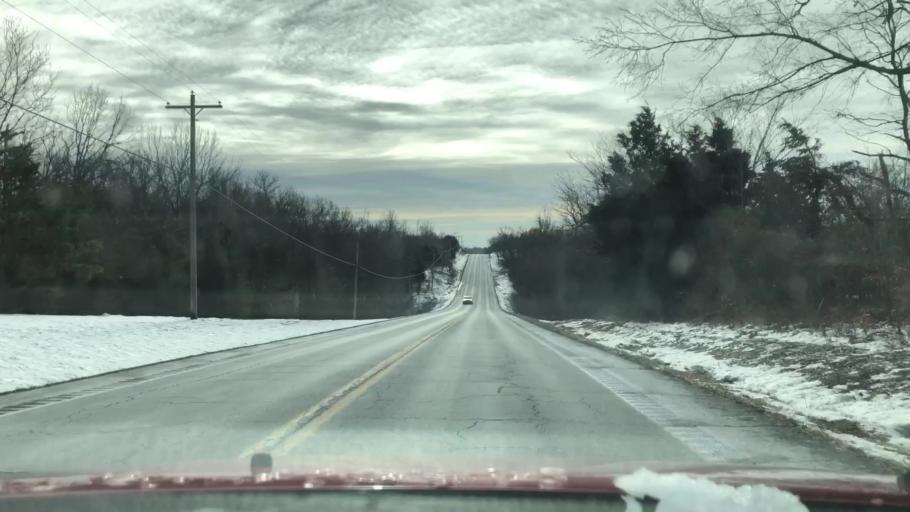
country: US
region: Missouri
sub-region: Jackson County
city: Oak Grove
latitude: 38.9682
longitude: -94.1309
